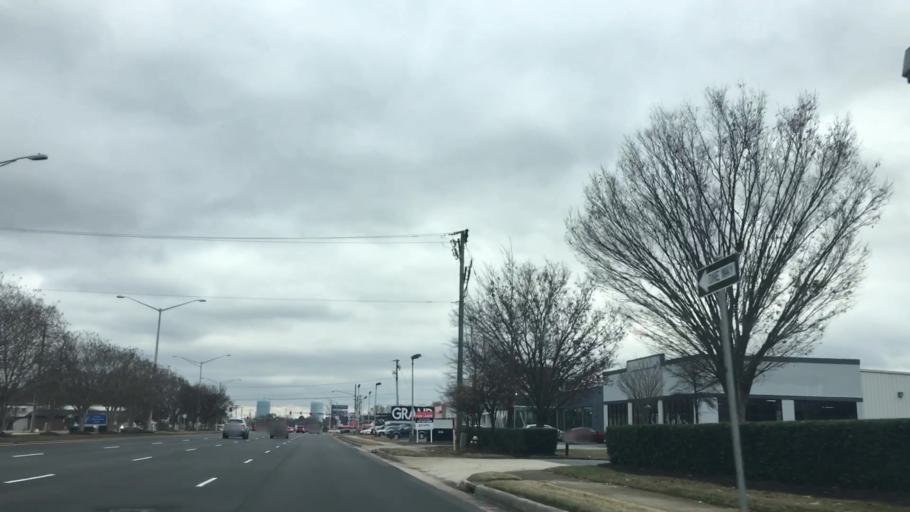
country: US
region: Virginia
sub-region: City of Chesapeake
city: Chesapeake
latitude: 36.8468
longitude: -76.1597
